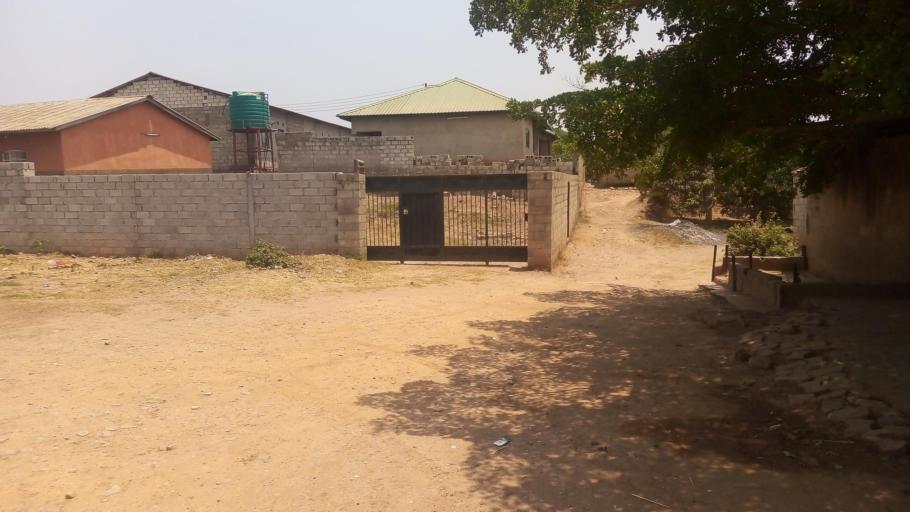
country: ZM
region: Lusaka
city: Lusaka
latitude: -15.4393
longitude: 28.3759
